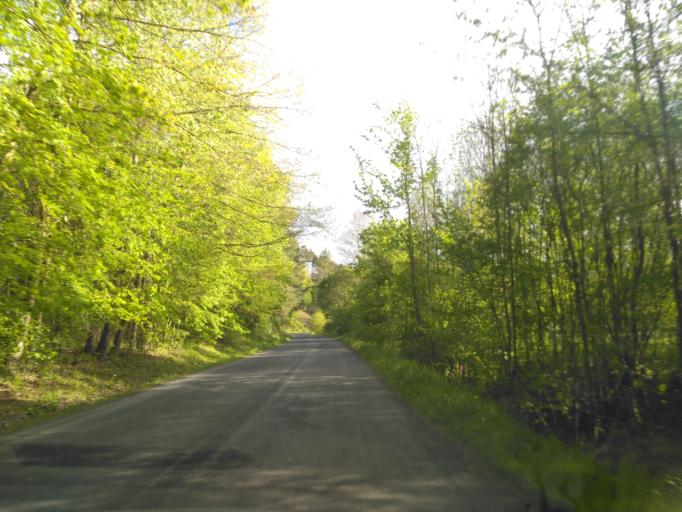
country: CZ
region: Central Bohemia
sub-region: Okres Beroun
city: Kraluv Dvur
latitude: 49.9282
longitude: 14.0485
